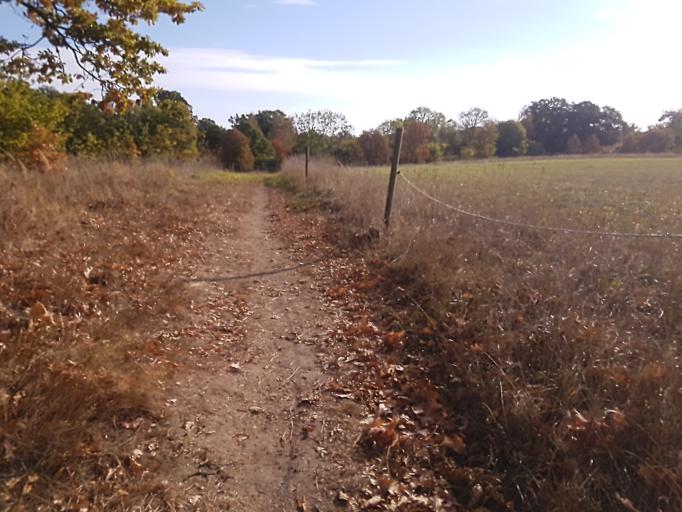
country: SE
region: Kronoberg
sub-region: Vaxjo Kommun
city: Vaexjoe
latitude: 56.8473
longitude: 14.8308
